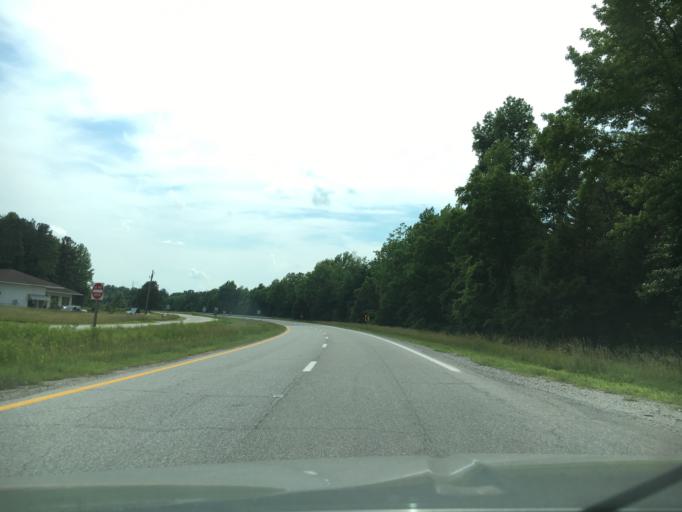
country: US
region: Virginia
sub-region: Prince Edward County
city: Hampden Sydney
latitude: 37.1057
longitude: -78.3675
